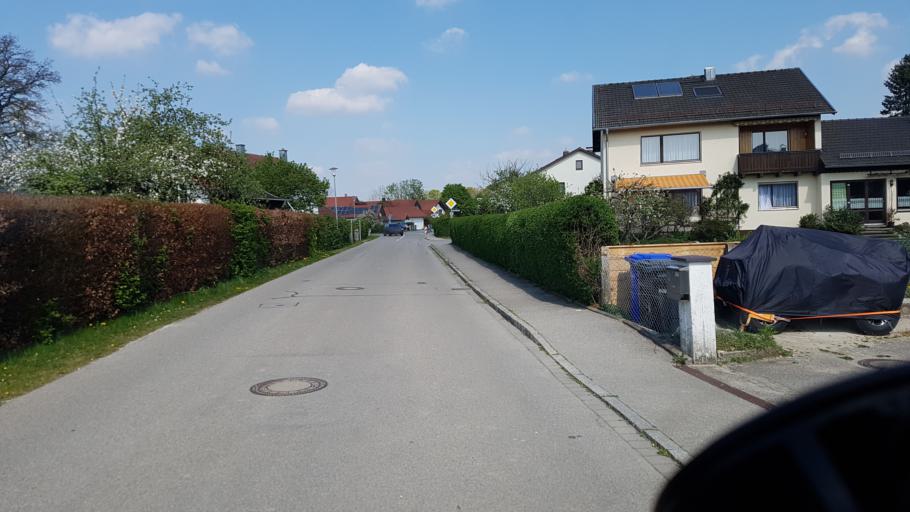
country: DE
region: Bavaria
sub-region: Upper Bavaria
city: Perach
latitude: 48.2428
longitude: 12.7470
